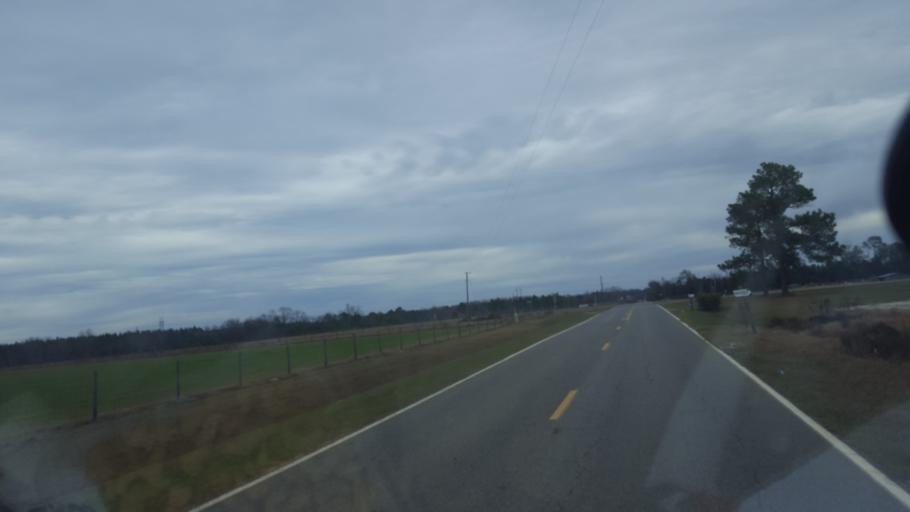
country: US
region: Georgia
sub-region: Ben Hill County
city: Fitzgerald
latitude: 31.7438
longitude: -83.3111
